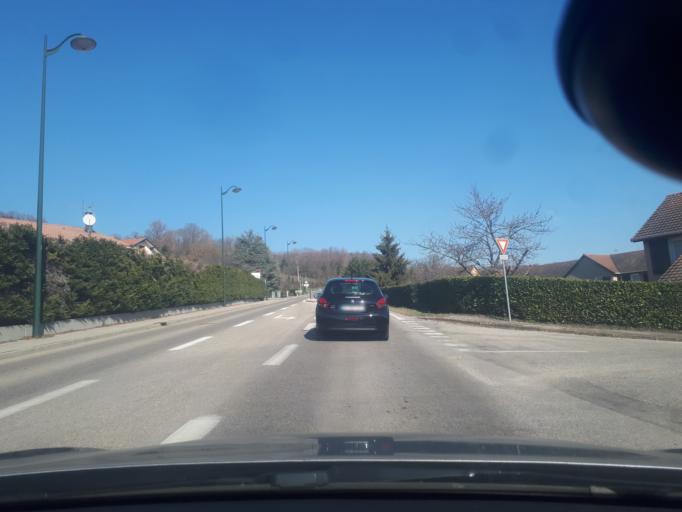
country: FR
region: Rhone-Alpes
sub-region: Departement de l'Isere
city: La Cote-Saint-Andre
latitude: 45.3977
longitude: 5.2707
